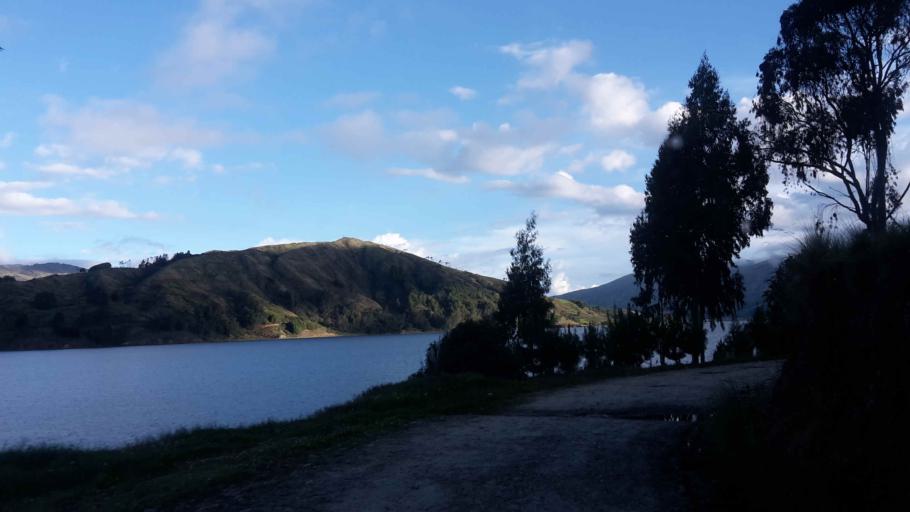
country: BO
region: Cochabamba
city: Colomi
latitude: -17.2638
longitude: -65.9049
